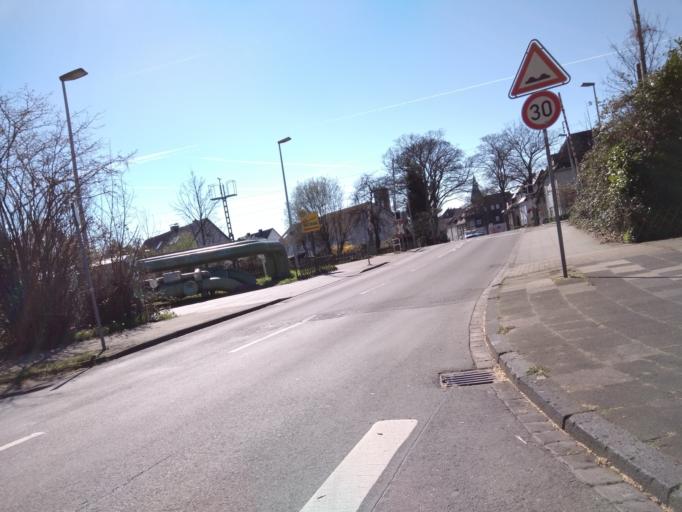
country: DE
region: North Rhine-Westphalia
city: Herten
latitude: 51.6045
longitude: 7.0942
